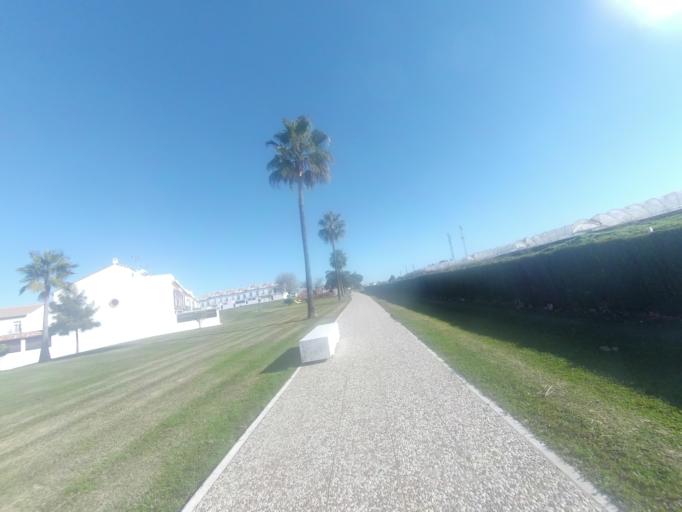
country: ES
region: Andalusia
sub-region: Provincia de Huelva
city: Palos de la Frontera
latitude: 37.2232
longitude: -6.9006
